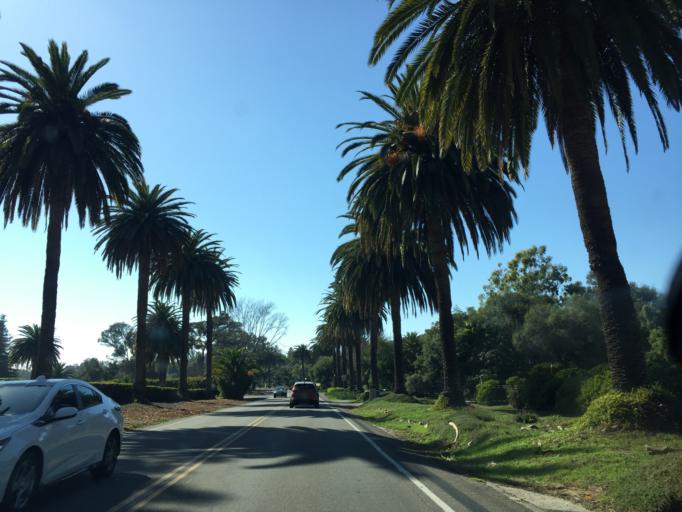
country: US
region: California
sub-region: Santa Barbara County
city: Mission Canyon
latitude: 34.4354
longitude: -119.7586
